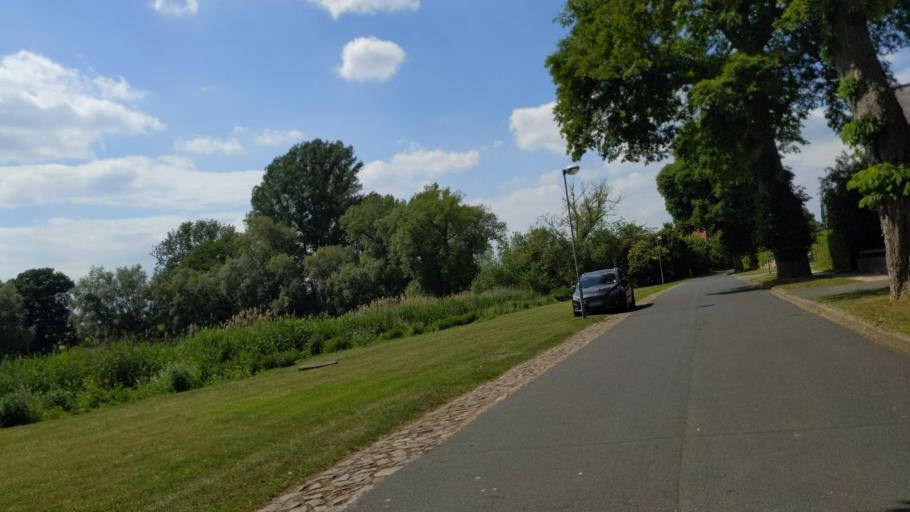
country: DE
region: Schleswig-Holstein
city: Kulpin
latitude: 53.7108
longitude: 10.6946
